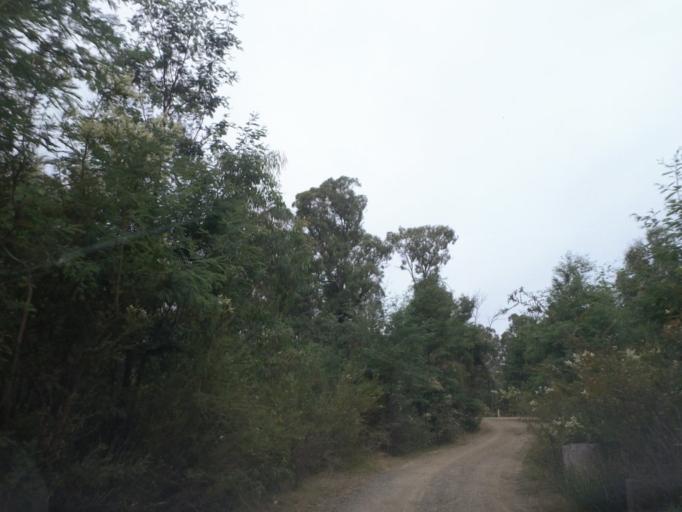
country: AU
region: Victoria
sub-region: Murrindindi
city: Alexandra
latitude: -37.3907
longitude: 145.5549
